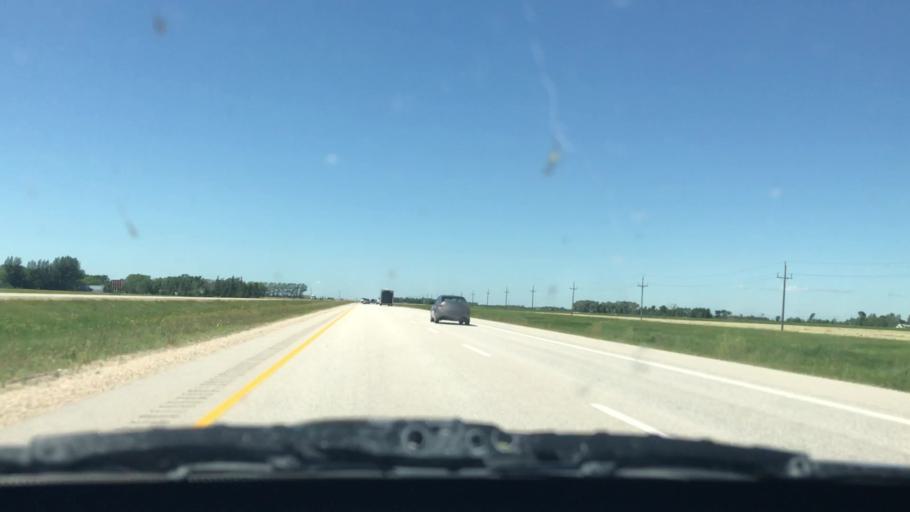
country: CA
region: Manitoba
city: Steinbach
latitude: 49.7295
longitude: -96.7168
